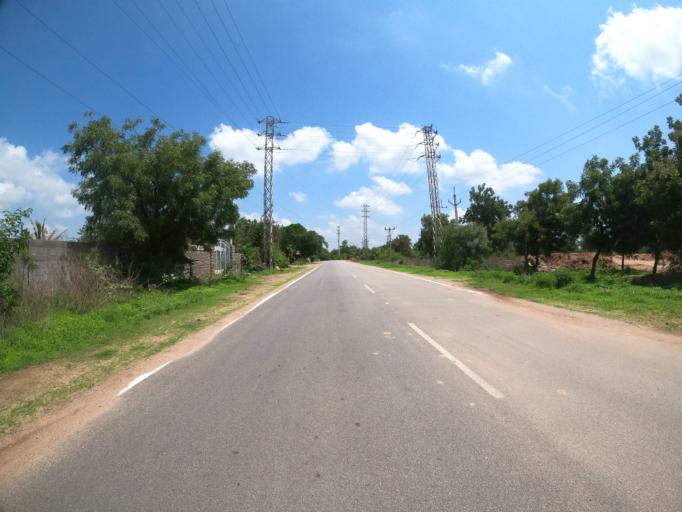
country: IN
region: Telangana
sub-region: Rangareddi
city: Sriramnagar
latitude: 17.3702
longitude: 78.3245
